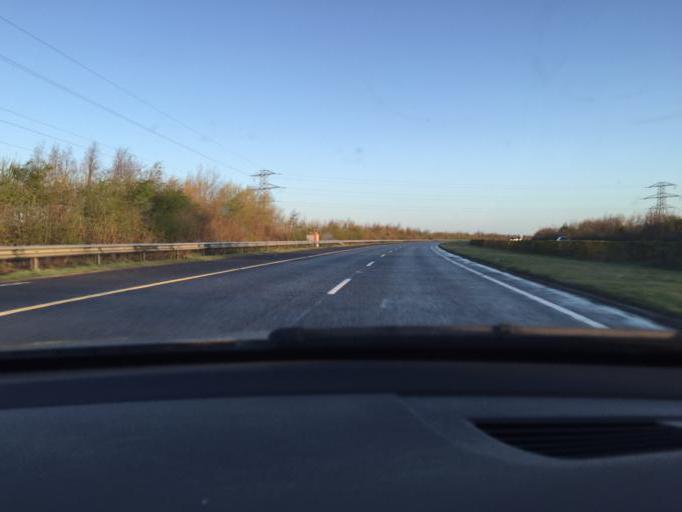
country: IE
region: Leinster
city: Lusk
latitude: 53.5133
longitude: -6.2067
